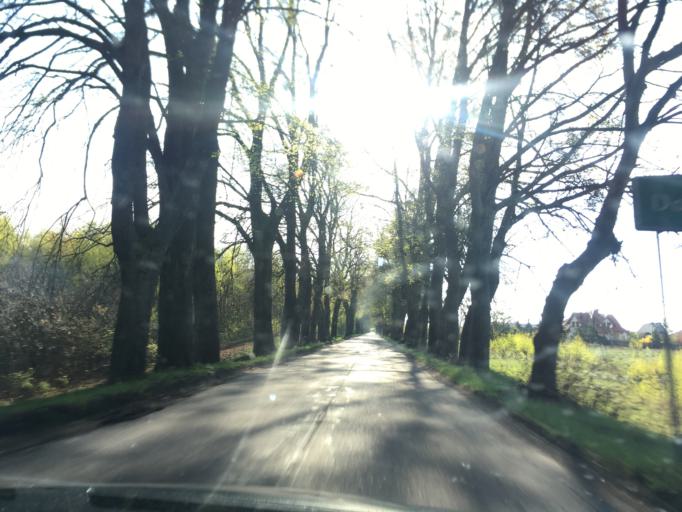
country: PL
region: Warmian-Masurian Voivodeship
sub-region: Powiat nidzicki
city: Nidzica
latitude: 53.4336
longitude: 20.3704
